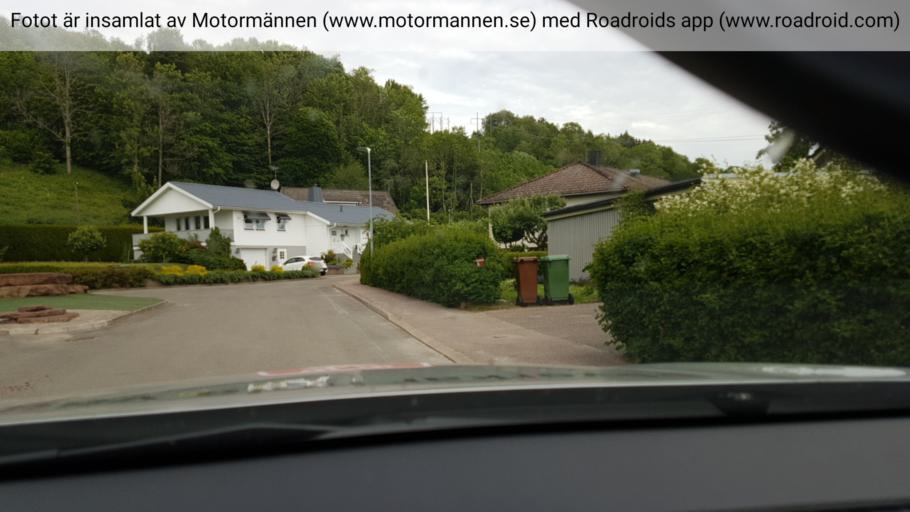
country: SE
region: Vaestra Goetaland
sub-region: Falkopings Kommun
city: Falkoeping
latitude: 58.1730
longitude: 13.5293
